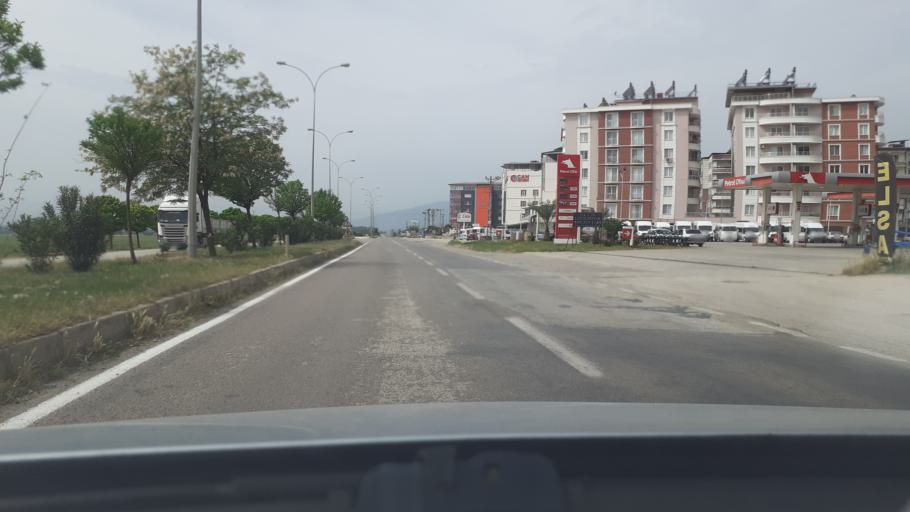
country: TR
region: Hatay
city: Kirikhan
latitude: 36.4808
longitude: 36.3576
